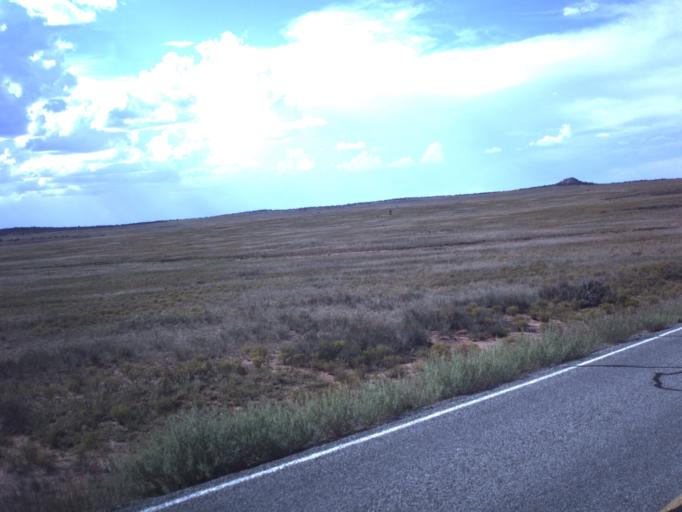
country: US
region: Utah
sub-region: Grand County
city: Moab
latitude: 38.5301
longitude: -109.7508
